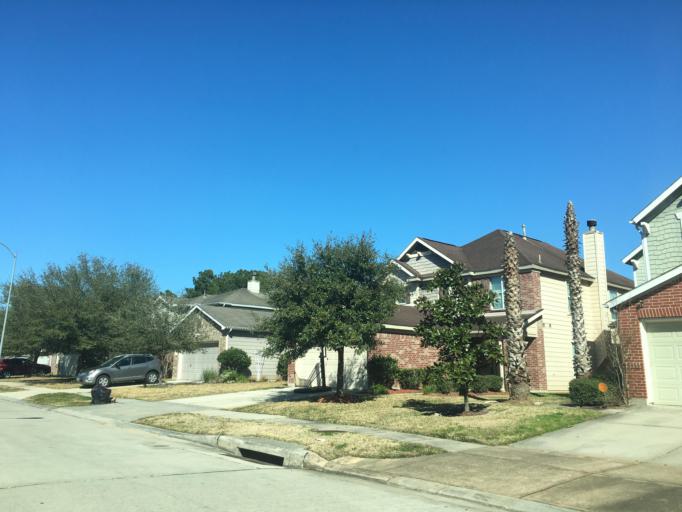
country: US
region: Texas
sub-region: Harris County
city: Spring
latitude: 30.0852
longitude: -95.4621
